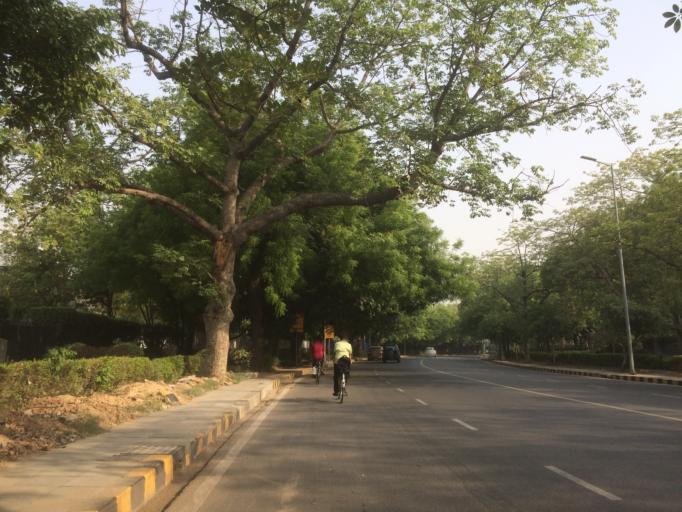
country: IN
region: NCT
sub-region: New Delhi
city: New Delhi
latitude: 28.5863
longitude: 77.1833
